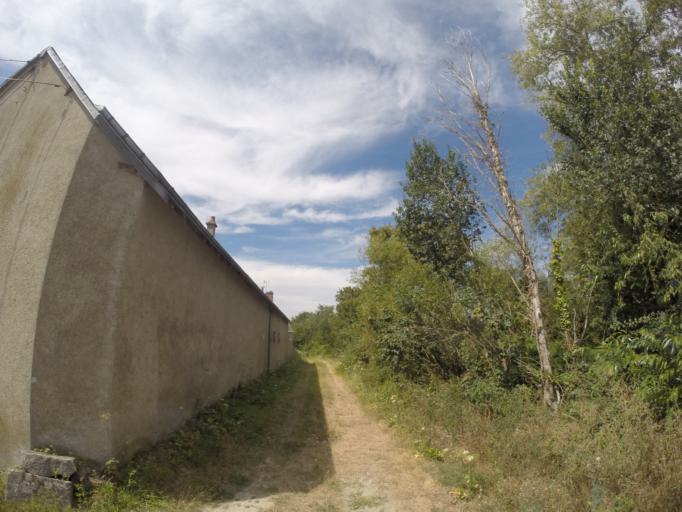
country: FR
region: Centre
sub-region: Departement d'Indre-et-Loire
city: Rochecorbon
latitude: 47.4203
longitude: 0.7190
